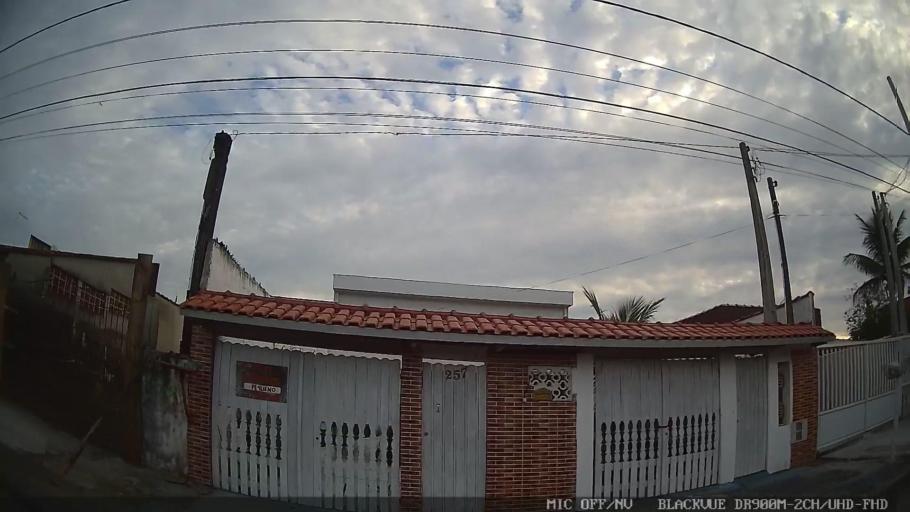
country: BR
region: Sao Paulo
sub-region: Itanhaem
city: Itanhaem
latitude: -24.1647
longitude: -46.7792
